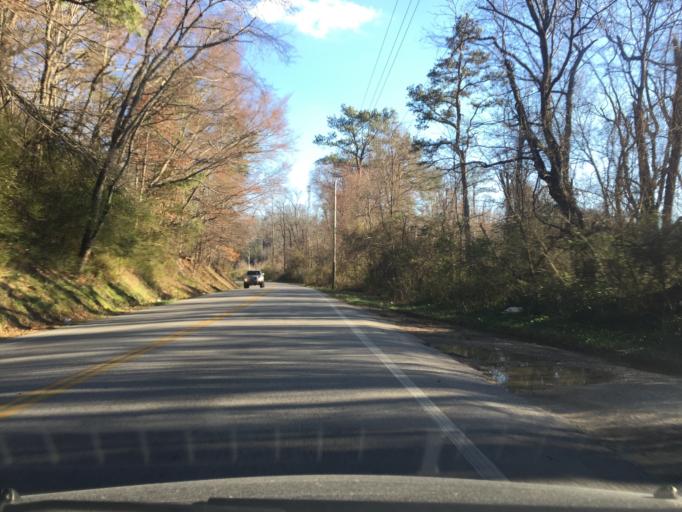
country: US
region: Tennessee
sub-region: Hamilton County
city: Harrison
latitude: 35.1393
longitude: -85.1204
